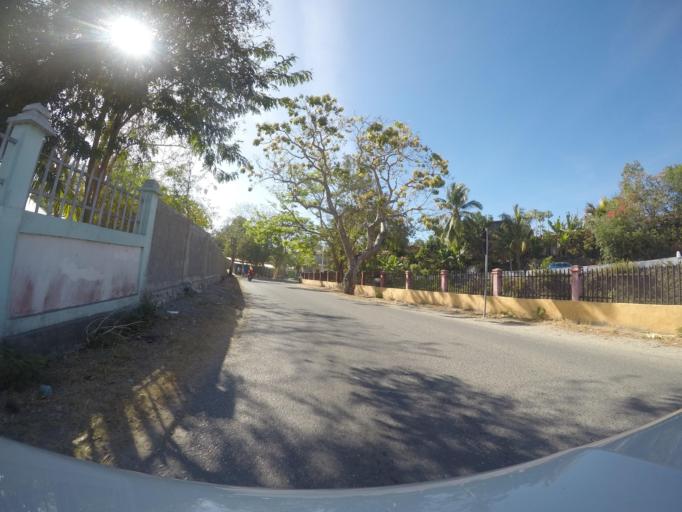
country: TL
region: Baucau
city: Baucau
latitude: -8.4659
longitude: 126.4609
